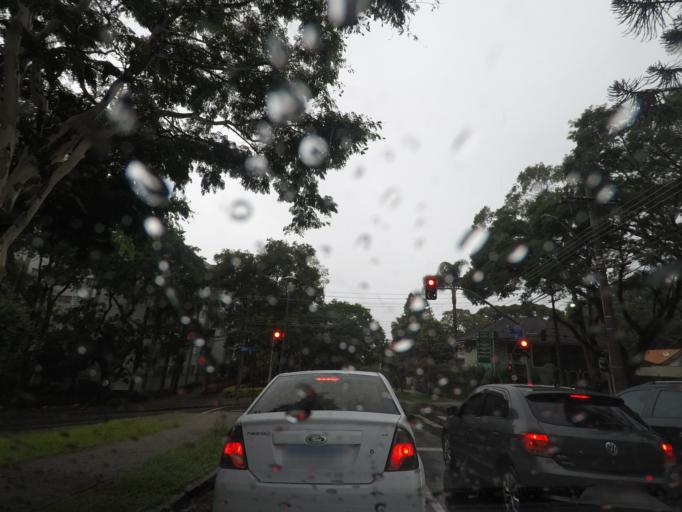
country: BR
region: Parana
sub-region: Curitiba
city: Curitiba
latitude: -25.4236
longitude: -49.2886
